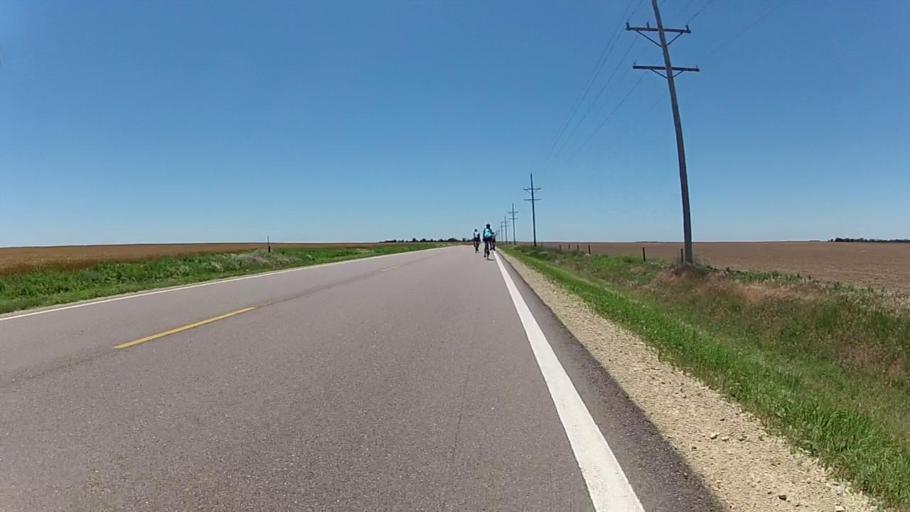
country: US
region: Kansas
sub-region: Kiowa County
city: Greensburg
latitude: 37.5265
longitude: -99.3207
